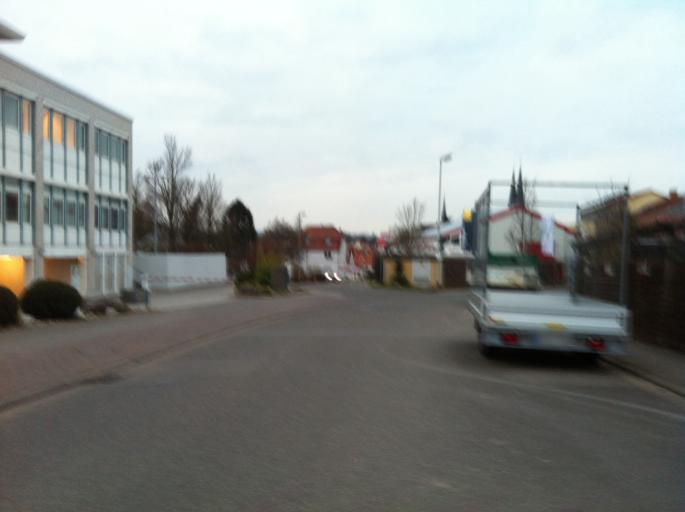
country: DE
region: Rheinland-Pfalz
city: Budenheim
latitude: 49.9960
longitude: 8.2091
